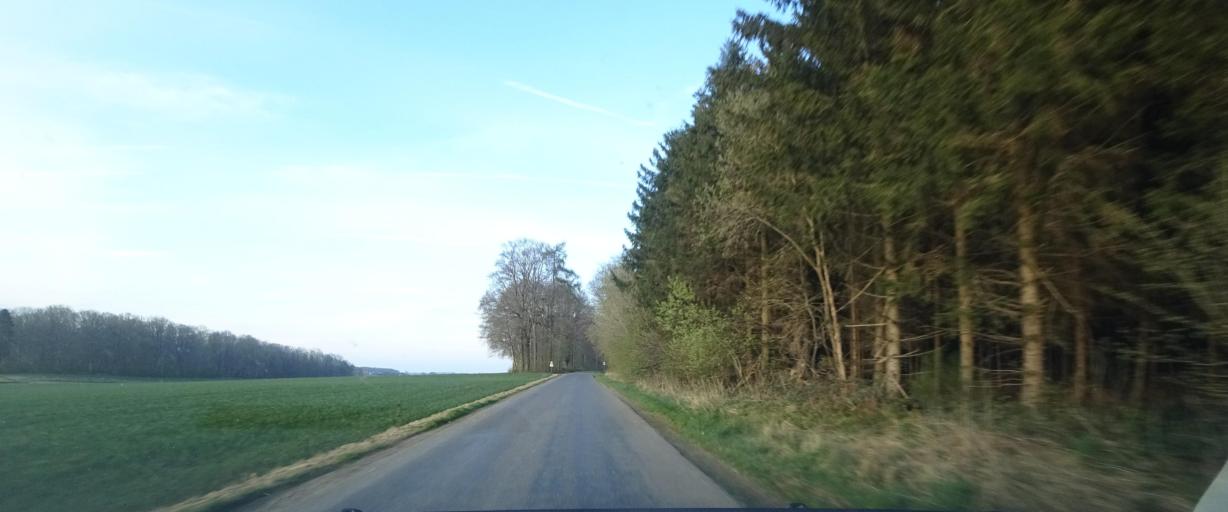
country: BE
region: Wallonia
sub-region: Province de Namur
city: Hamois
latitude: 50.3292
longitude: 5.2147
